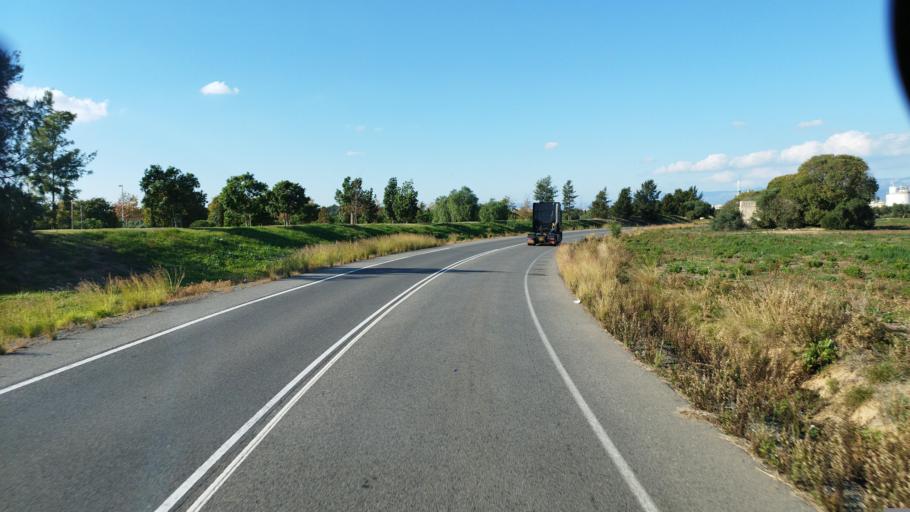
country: ES
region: Catalonia
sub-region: Provincia de Tarragona
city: Vila-seca
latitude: 41.0979
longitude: 1.1691
